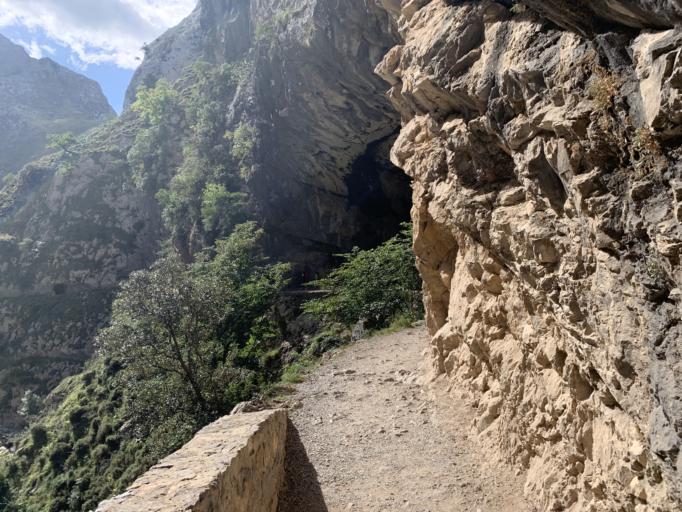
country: ES
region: Castille and Leon
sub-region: Provincia de Leon
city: Posada de Valdeon
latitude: 43.2246
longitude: -4.8966
